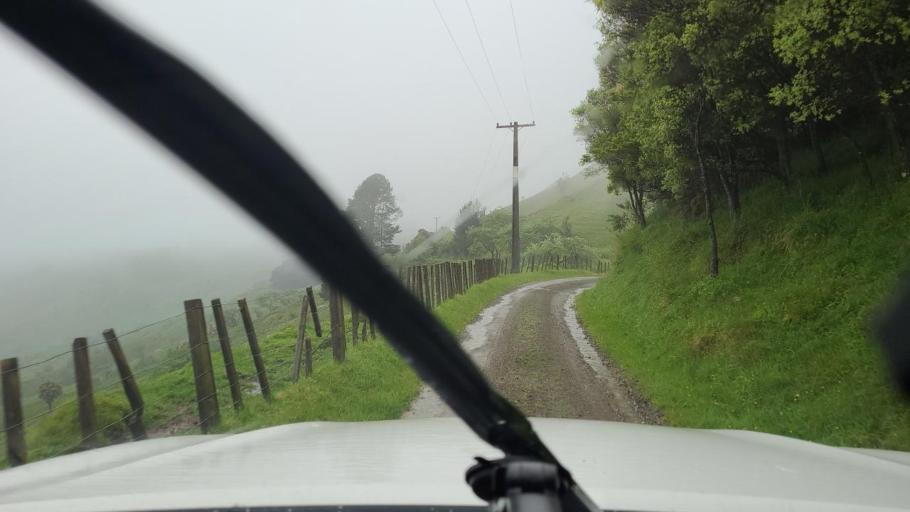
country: NZ
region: Gisborne
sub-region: Gisborne District
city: Gisborne
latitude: -38.4854
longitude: 177.6180
